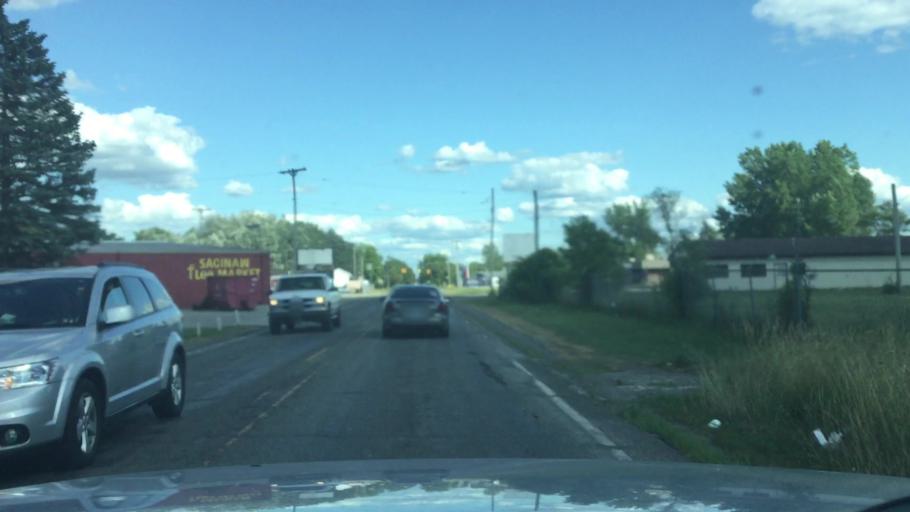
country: US
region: Michigan
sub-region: Saginaw County
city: Saginaw
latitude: 43.3927
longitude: -83.9384
